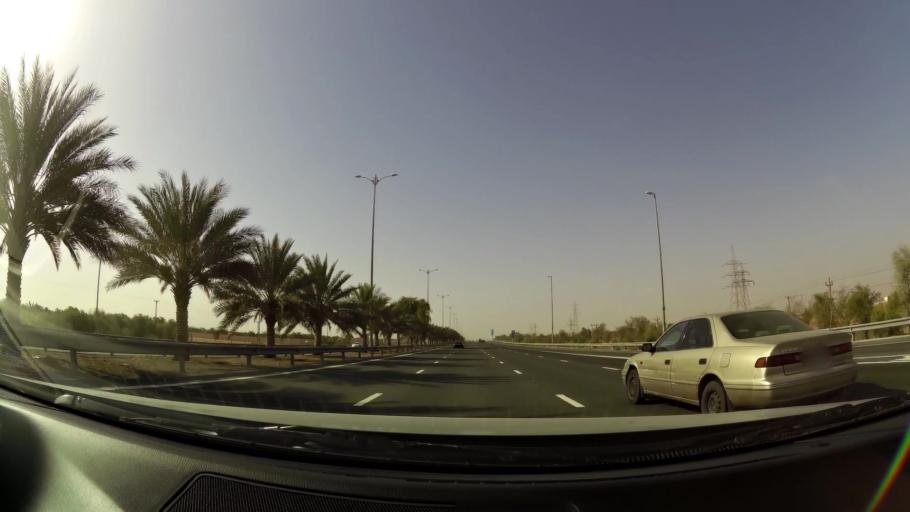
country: OM
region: Al Buraimi
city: Al Buraymi
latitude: 24.4783
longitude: 55.7753
